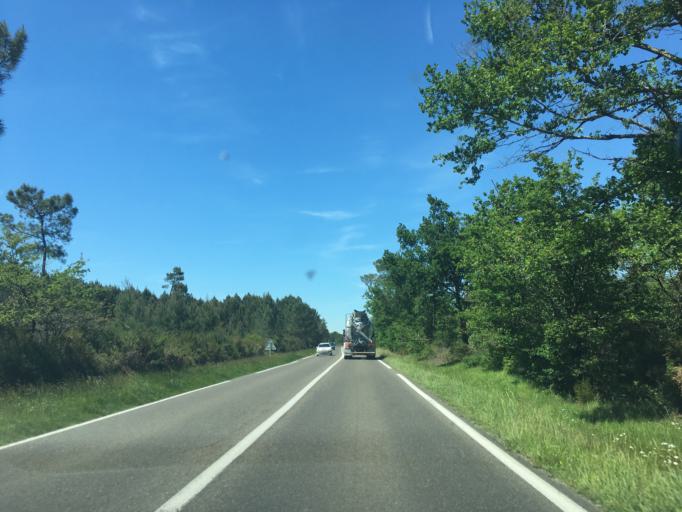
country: FR
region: Aquitaine
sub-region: Departement de la Gironde
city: Listrac-Medoc
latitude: 45.0976
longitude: -0.8009
